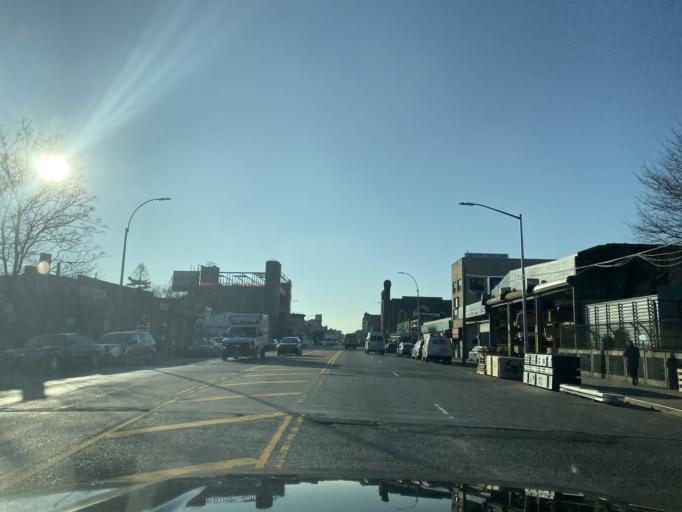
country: US
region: New York
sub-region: Kings County
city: Brooklyn
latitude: 40.6288
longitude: -73.9660
